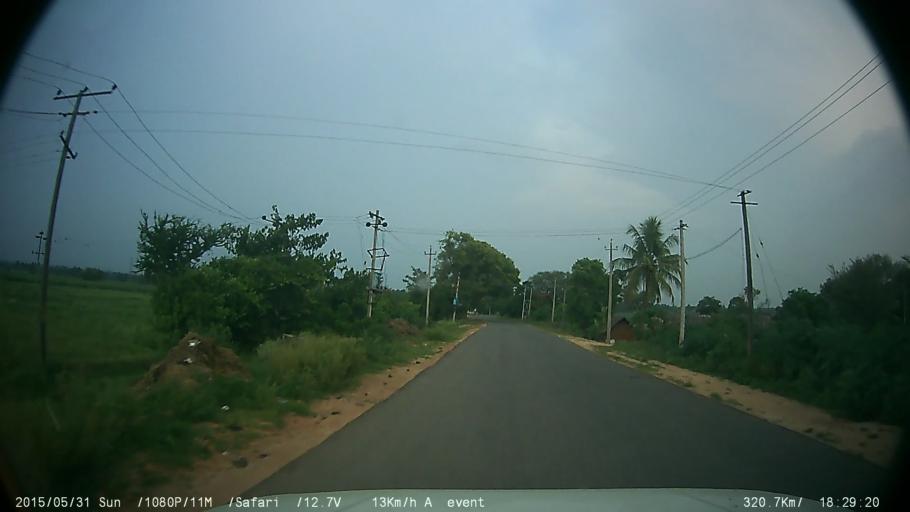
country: IN
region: Karnataka
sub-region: Mysore
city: Nanjangud
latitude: 12.1221
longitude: 76.7299
